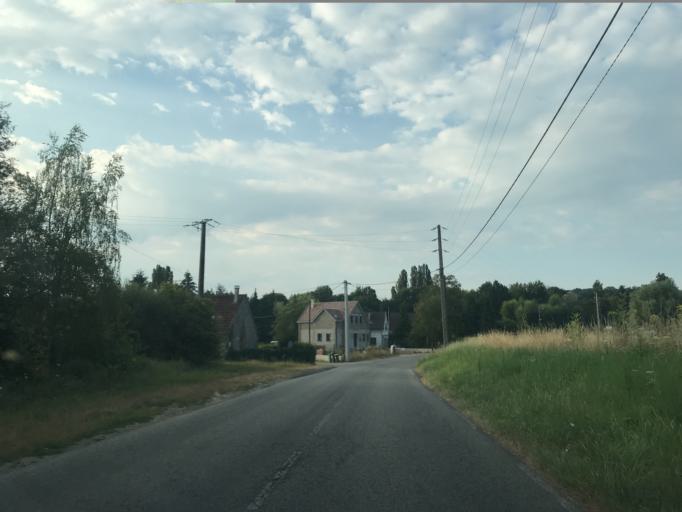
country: FR
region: Ile-de-France
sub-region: Departement des Yvelines
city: Jouars-Pontchartrain
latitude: 48.7625
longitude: 1.8844
